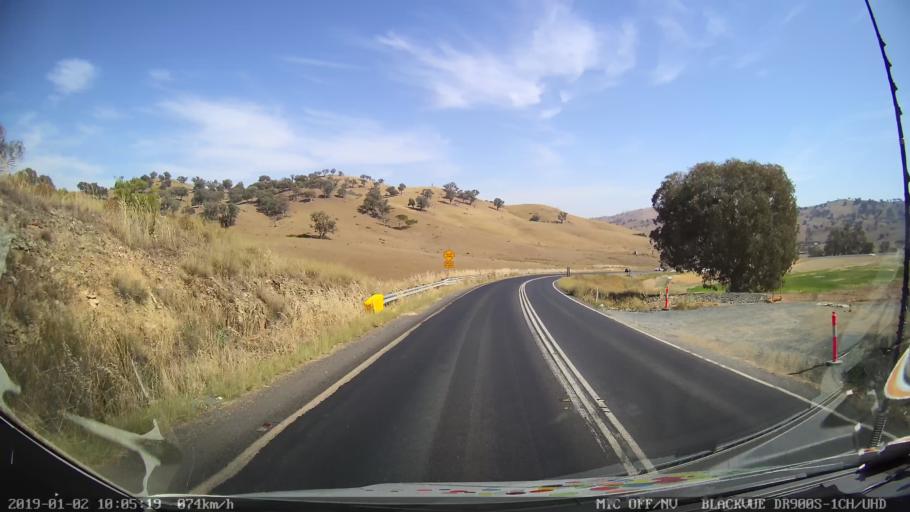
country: AU
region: New South Wales
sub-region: Gundagai
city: Gundagai
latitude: -35.1604
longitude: 148.1169
